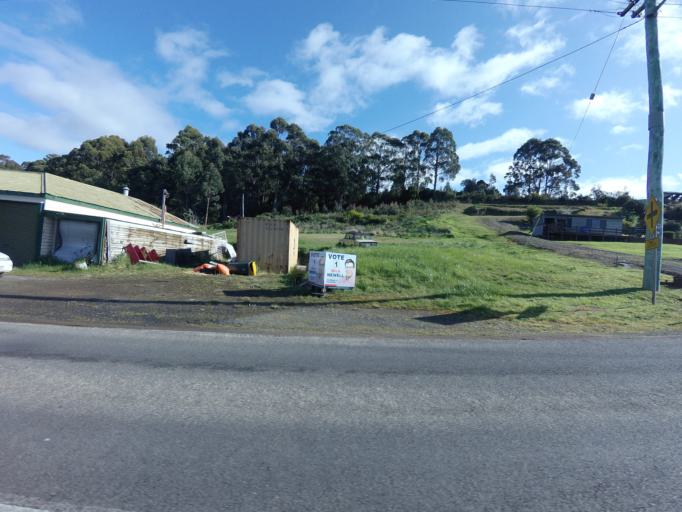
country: AU
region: Tasmania
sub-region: Huon Valley
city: Cygnet
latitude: -43.3150
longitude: 147.0134
